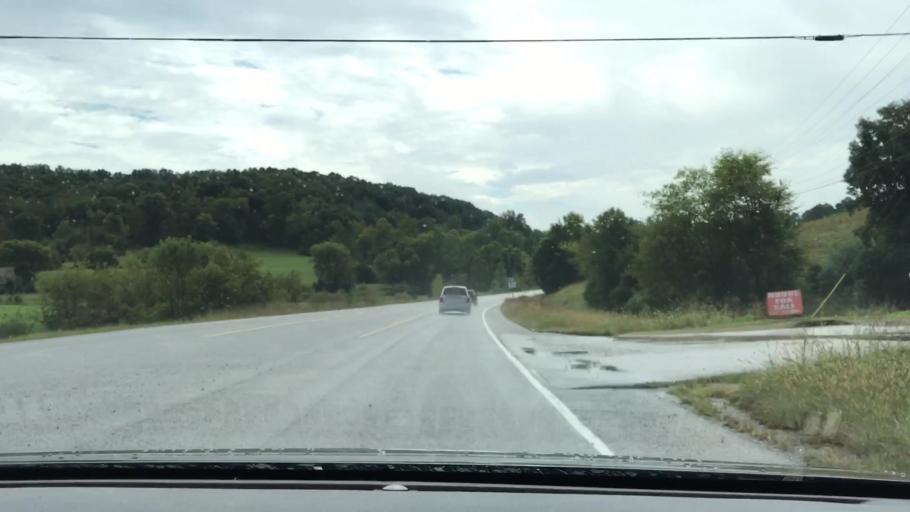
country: US
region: Tennessee
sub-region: Smith County
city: South Carthage
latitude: 36.2043
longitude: -85.9519
